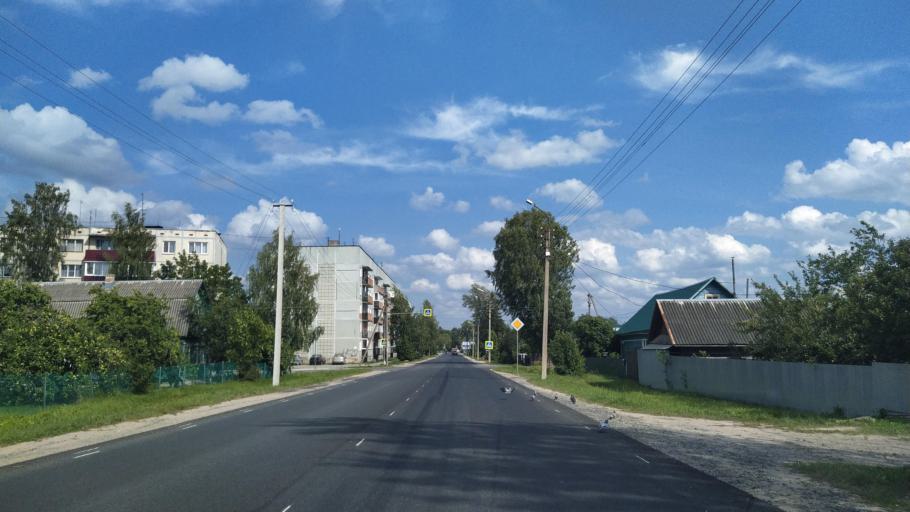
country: RU
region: Pskov
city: Porkhov
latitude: 57.7608
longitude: 29.5499
